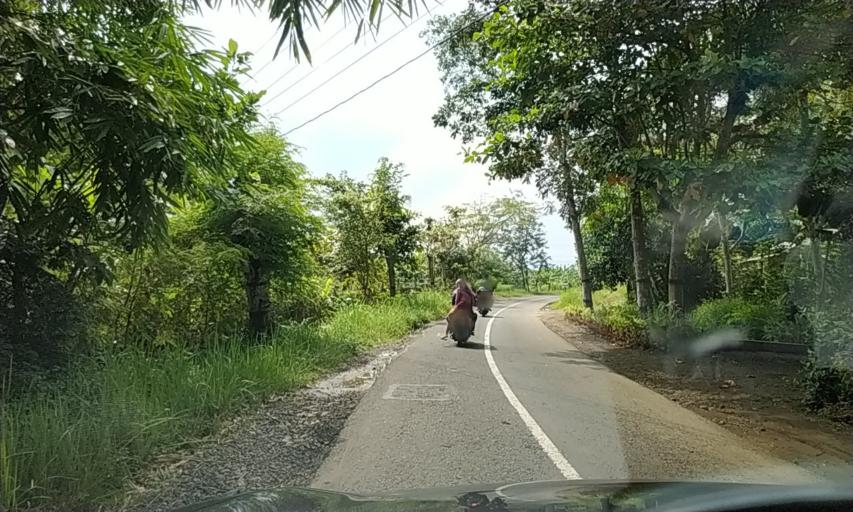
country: ID
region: Central Java
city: Meluwung
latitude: -7.3776
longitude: 108.7003
